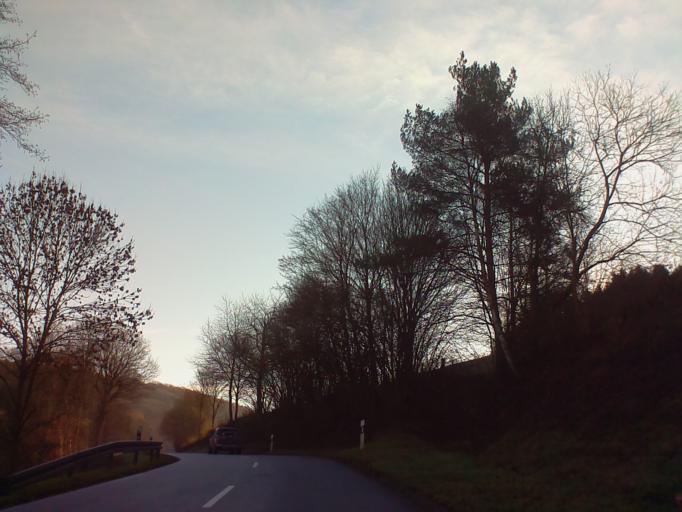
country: DE
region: Hesse
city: Reichelsheim
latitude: 49.6930
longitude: 8.8627
